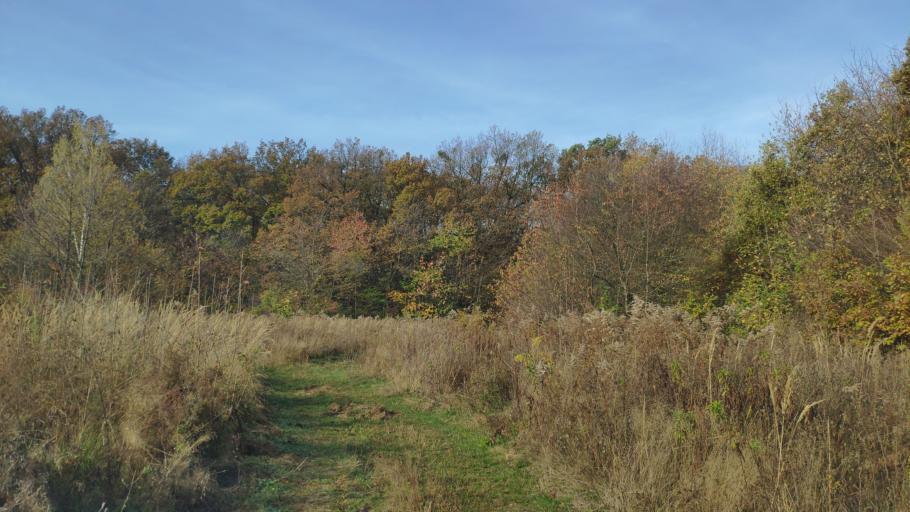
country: SK
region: Kosicky
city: Kosice
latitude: 48.7469
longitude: 21.2206
